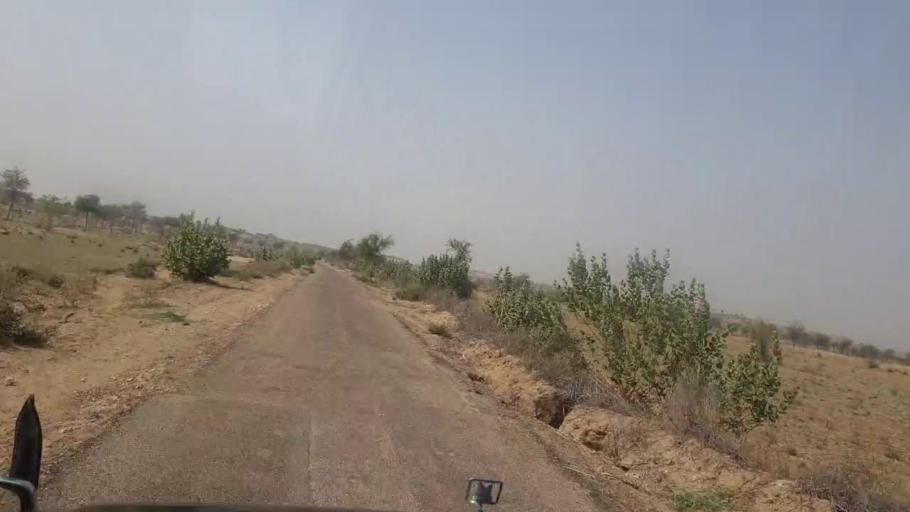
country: PK
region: Sindh
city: Islamkot
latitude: 25.0909
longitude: 70.1632
